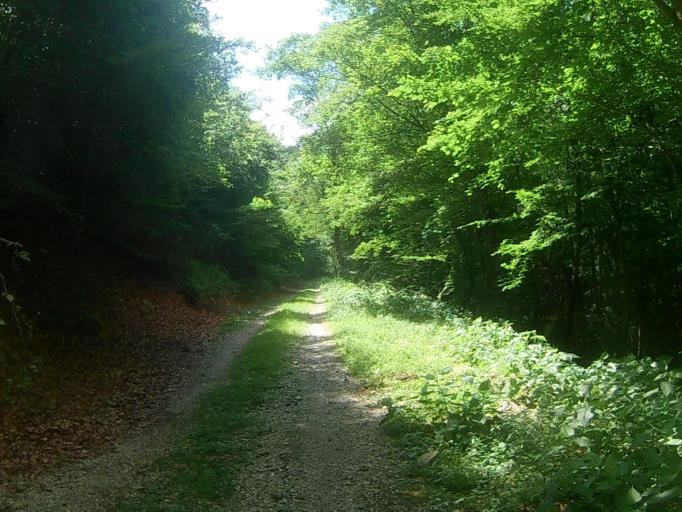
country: SI
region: Selnica ob Dravi
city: Selnica ob Dravi
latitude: 46.5207
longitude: 15.4896
